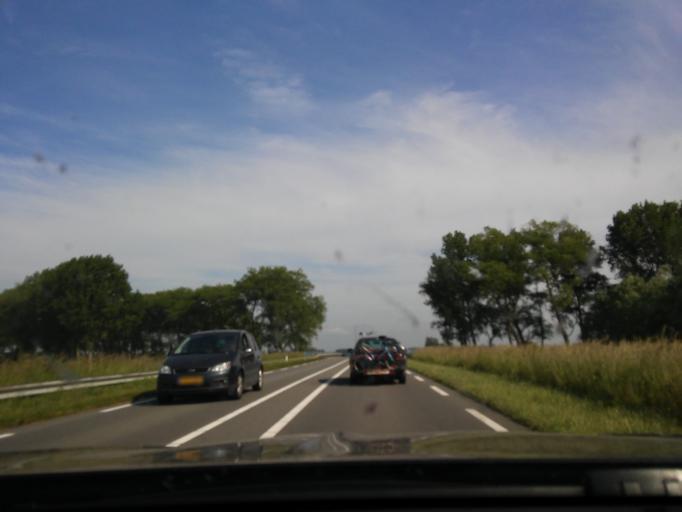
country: NL
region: Zeeland
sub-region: Gemeente Sluis
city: Sluis
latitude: 51.3066
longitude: 3.3717
